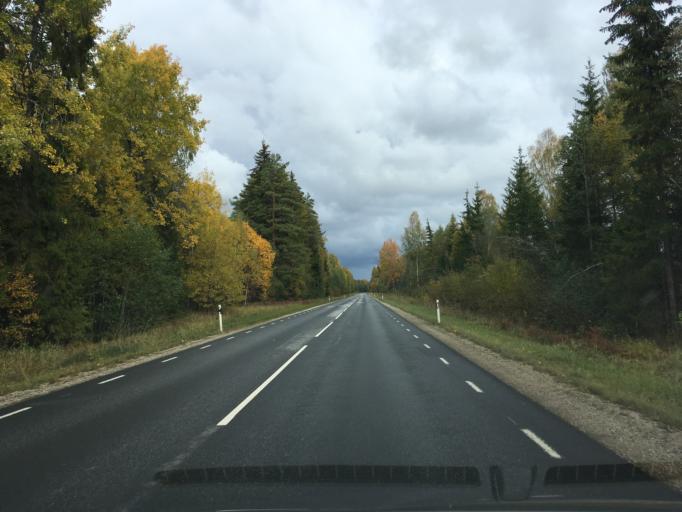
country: EE
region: Harju
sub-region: Anija vald
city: Kehra
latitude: 59.2645
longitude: 25.3531
